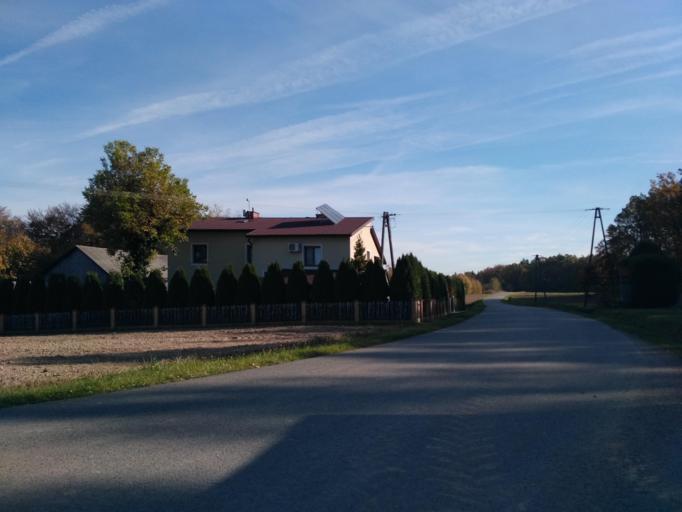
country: PL
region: Subcarpathian Voivodeship
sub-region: Powiat ropczycko-sedziszowski
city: Zagorzyce
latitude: 49.9967
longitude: 21.7174
